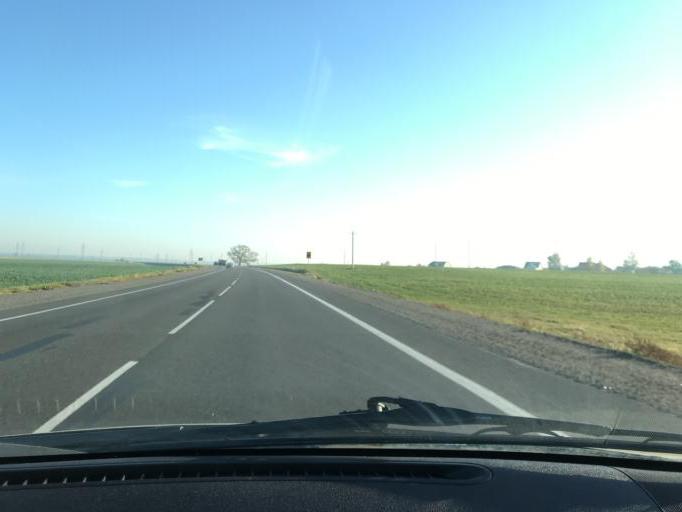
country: BY
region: Brest
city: Asnyezhytsy
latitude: 52.1908
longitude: 26.1000
